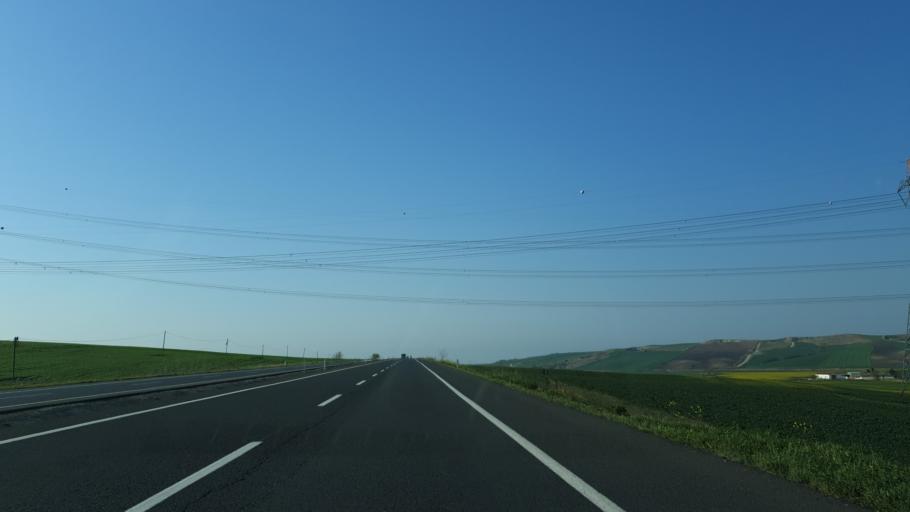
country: TR
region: Tekirdag
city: Corlu
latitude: 41.0722
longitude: 27.7405
